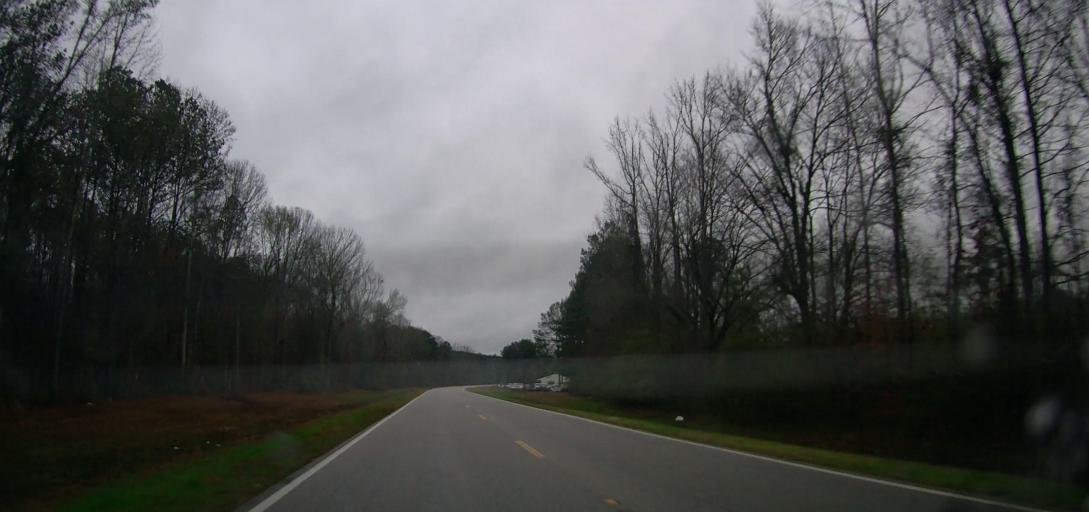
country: US
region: Alabama
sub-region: Bibb County
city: Centreville
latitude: 32.9214
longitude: -87.0352
